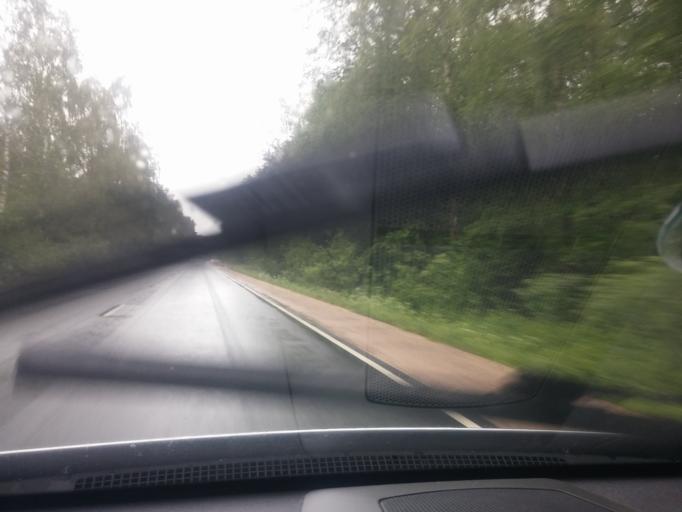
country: LV
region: Ikskile
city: Ikskile
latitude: 56.8905
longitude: 24.4775
